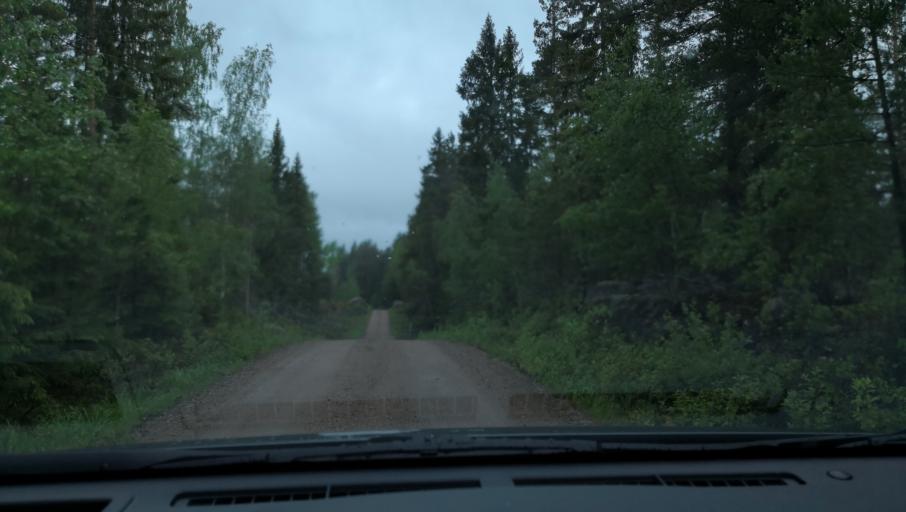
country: SE
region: Uppsala
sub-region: Enkopings Kommun
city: Orsundsbro
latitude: 59.9353
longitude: 17.3209
